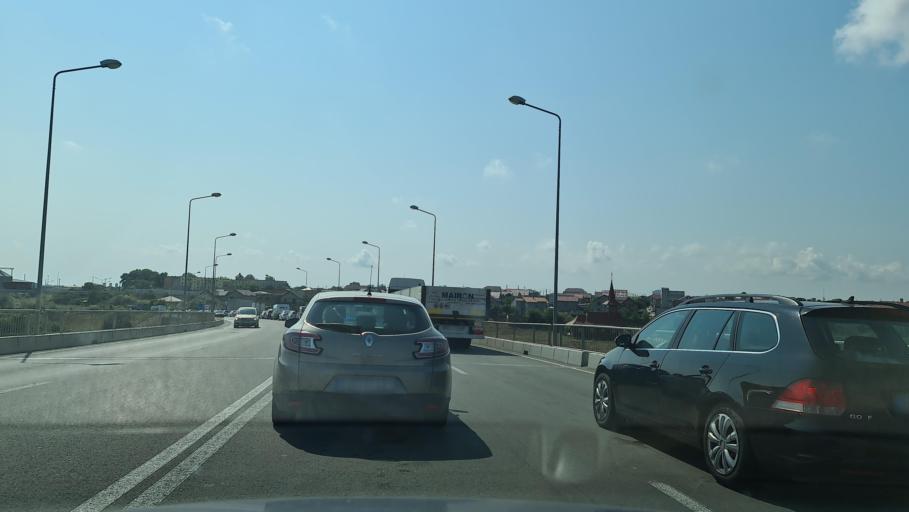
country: RO
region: Constanta
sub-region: Comuna Agigea
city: Agigea
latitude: 44.0976
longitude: 28.6351
